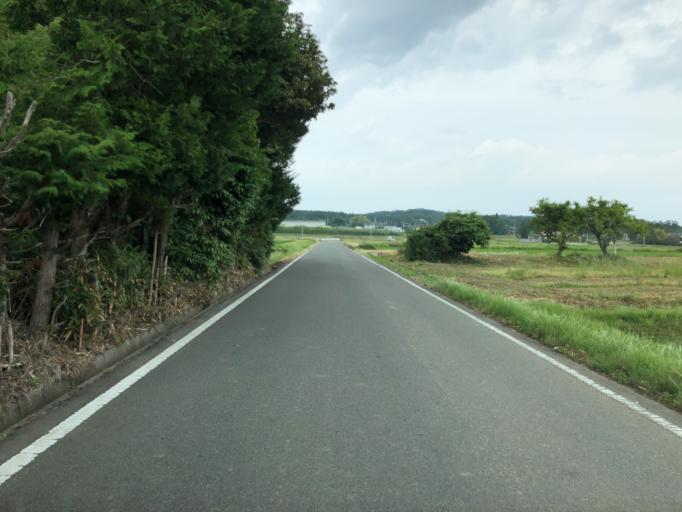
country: JP
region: Miyagi
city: Marumori
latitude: 37.7650
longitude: 140.9352
